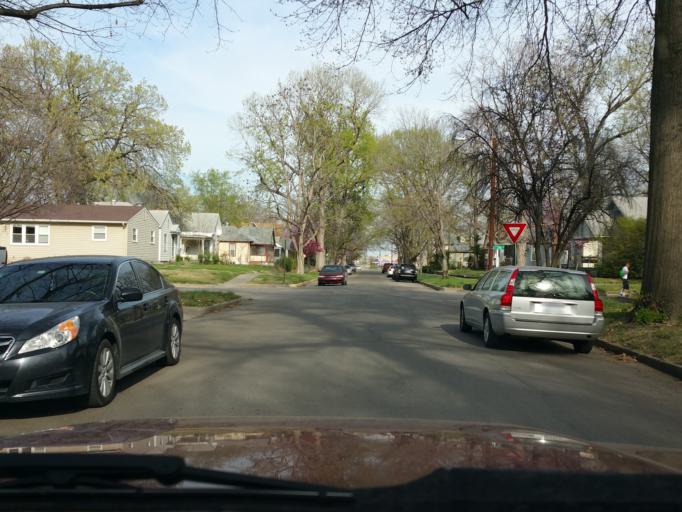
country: US
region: Kansas
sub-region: Riley County
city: Manhattan
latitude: 39.1878
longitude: -96.5638
